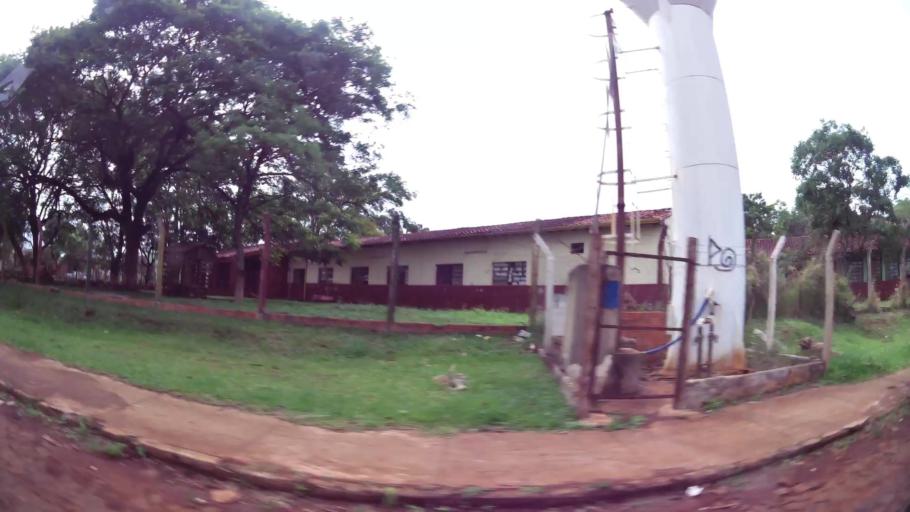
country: PY
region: Alto Parana
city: Ciudad del Este
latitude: -25.3938
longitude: -54.6387
